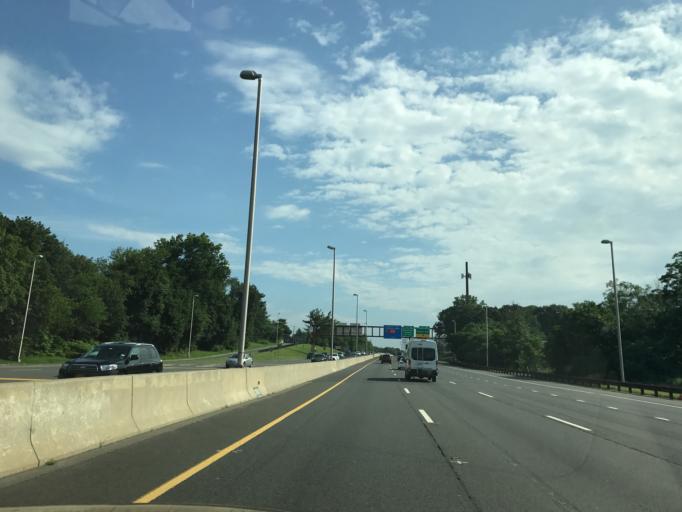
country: US
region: New Jersey
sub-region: Essex County
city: Bloomfield
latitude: 40.8060
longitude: -74.1833
